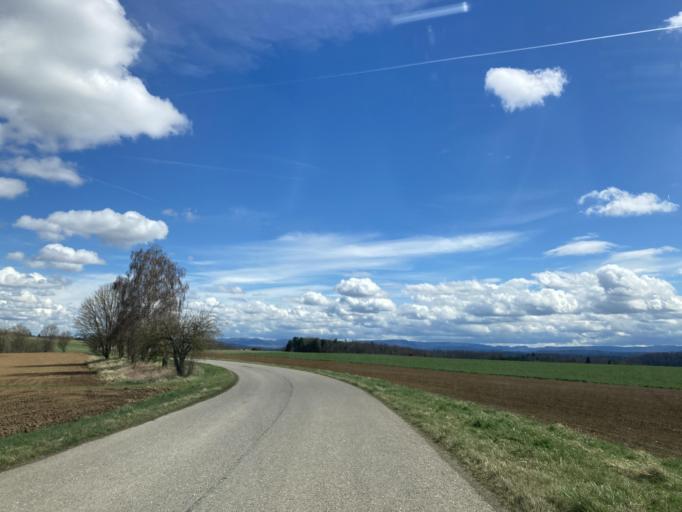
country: DE
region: Baden-Wuerttemberg
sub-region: Regierungsbezirk Stuttgart
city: Bondorf
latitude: 48.4572
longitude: 8.8347
